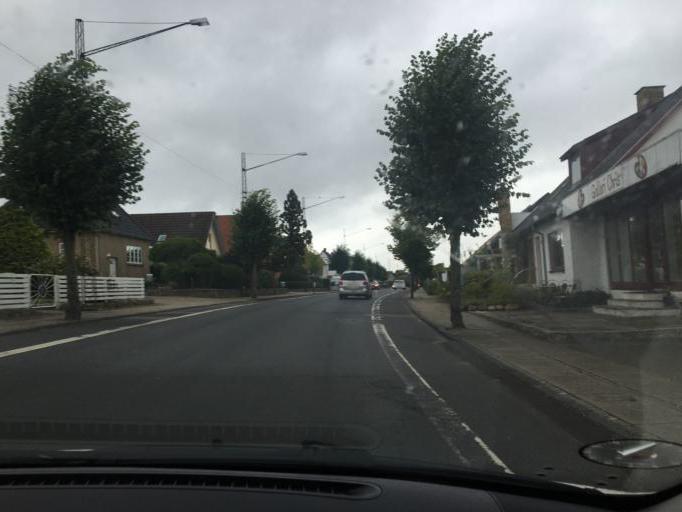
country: DK
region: South Denmark
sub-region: Middelfart Kommune
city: Middelfart
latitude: 55.4968
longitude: 9.7470
